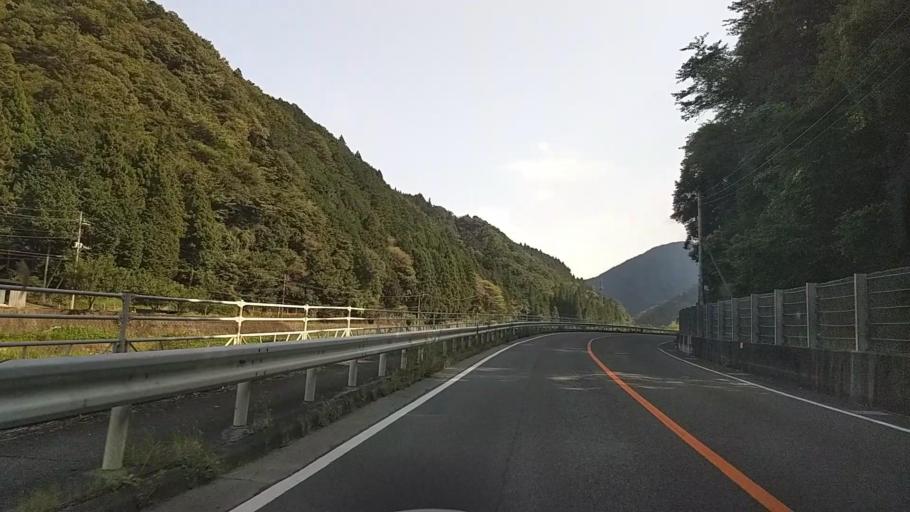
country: JP
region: Shizuoka
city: Fujinomiya
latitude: 35.3449
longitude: 138.4239
